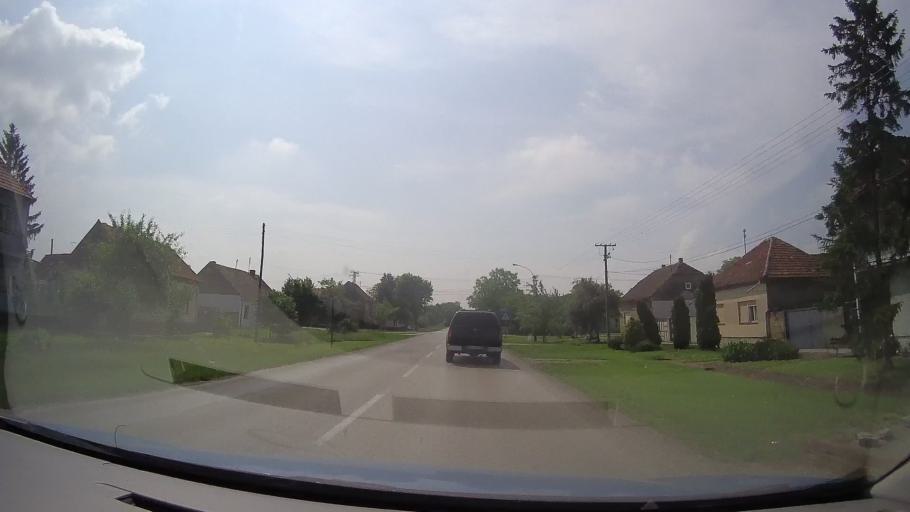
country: RS
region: Autonomna Pokrajina Vojvodina
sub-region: Juznobanatski Okrug
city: Kovacica
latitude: 45.1044
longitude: 20.6219
